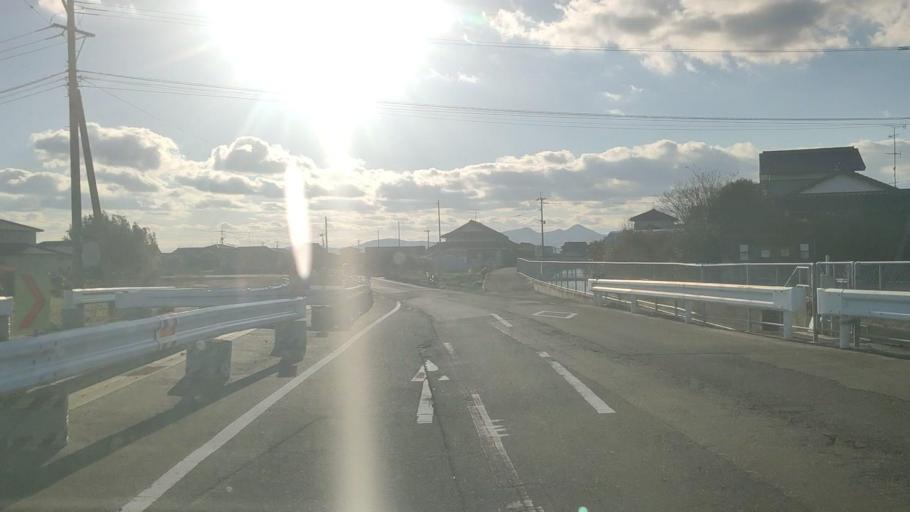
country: JP
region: Saga Prefecture
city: Saga-shi
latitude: 33.2962
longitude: 130.2434
